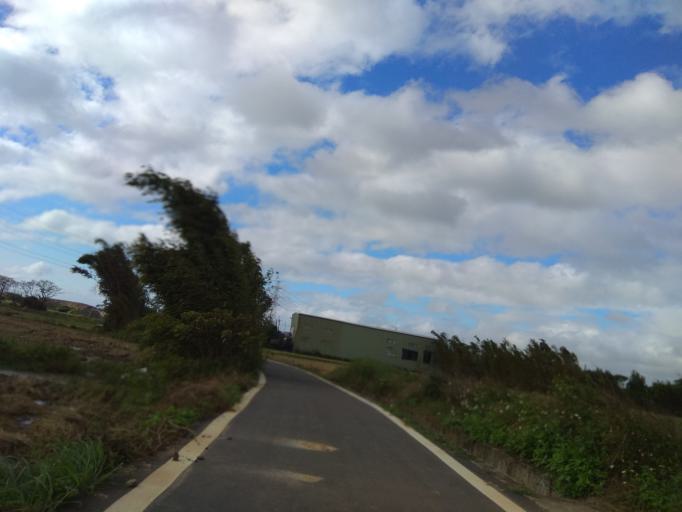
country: TW
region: Taiwan
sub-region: Hsinchu
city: Zhubei
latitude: 24.9697
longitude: 121.0805
